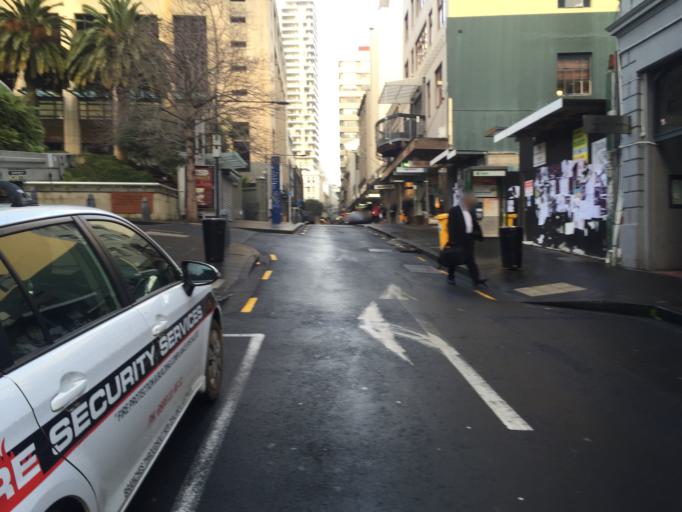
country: NZ
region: Auckland
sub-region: Auckland
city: Auckland
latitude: -36.8474
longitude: 174.7666
